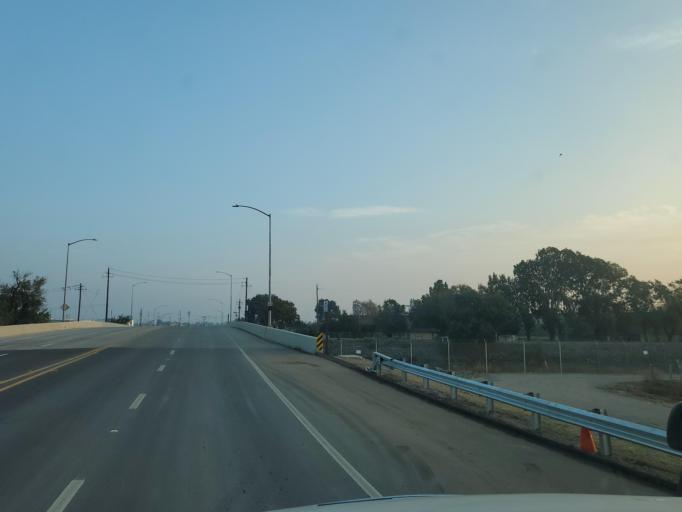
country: US
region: California
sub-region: San Joaquin County
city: Country Club
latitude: 37.9474
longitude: -121.3393
